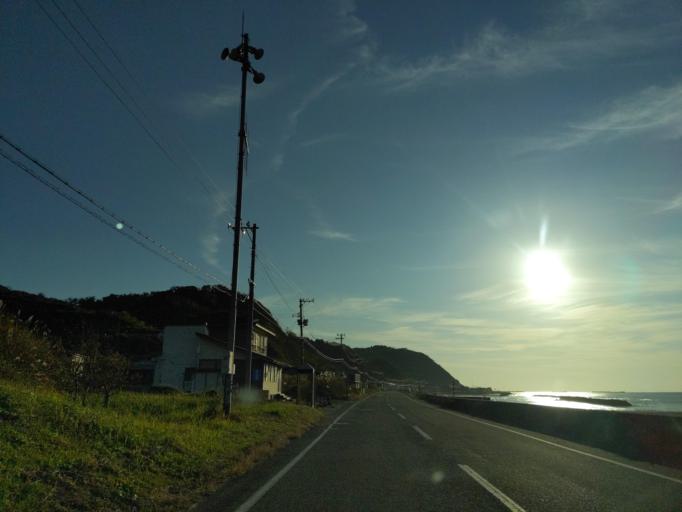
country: JP
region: Niigata
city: Nagaoka
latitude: 37.5574
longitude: 138.7122
